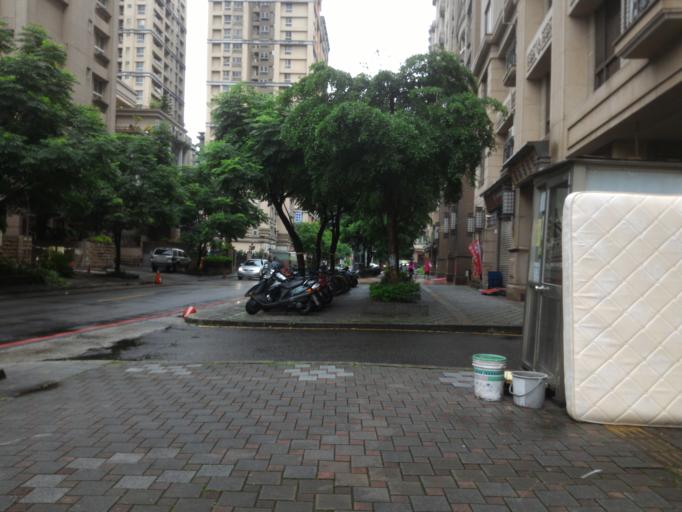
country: TW
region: Taiwan
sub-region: Taoyuan
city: Taoyuan
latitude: 24.9424
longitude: 121.3780
